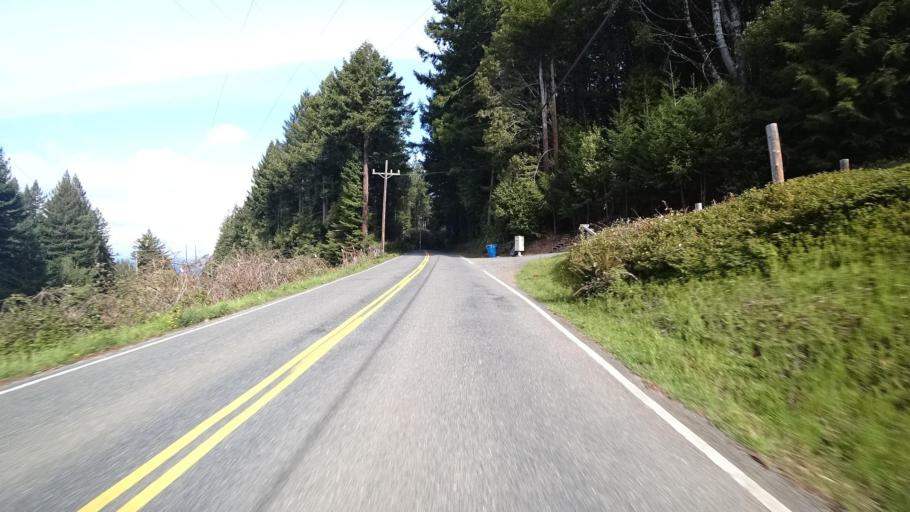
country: US
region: California
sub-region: Humboldt County
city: Bayside
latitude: 40.7589
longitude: -123.9926
